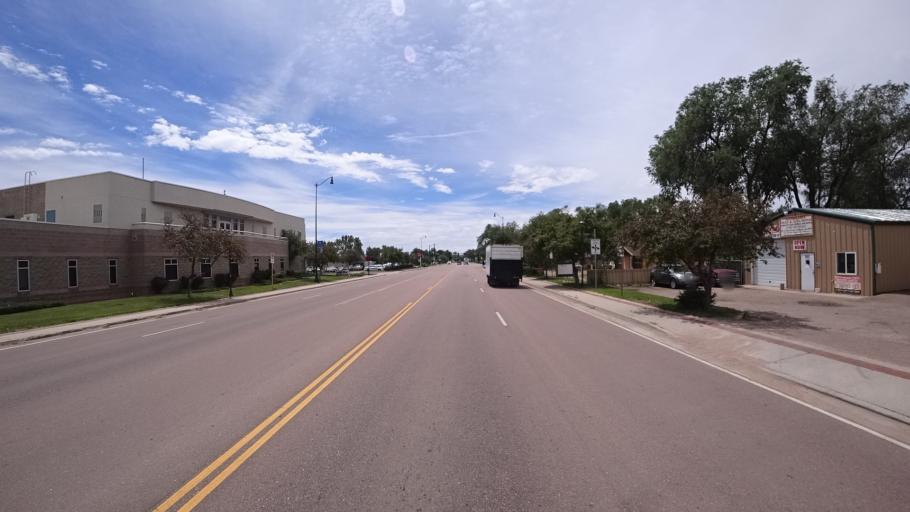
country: US
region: Colorado
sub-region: El Paso County
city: Fountain
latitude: 38.6851
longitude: -104.7047
